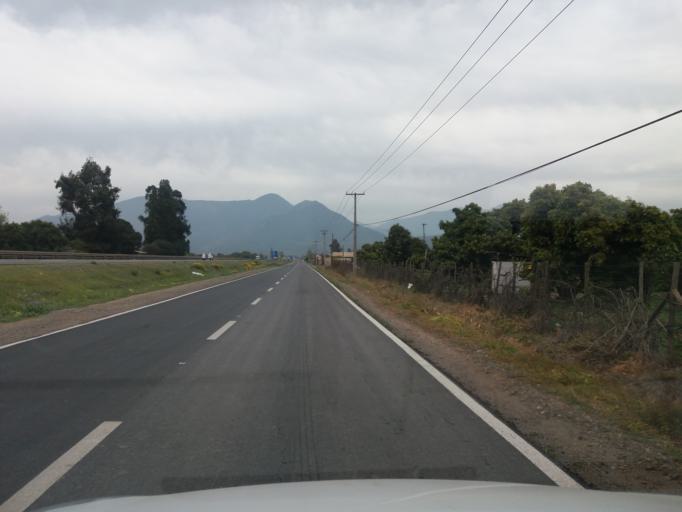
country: CL
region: Valparaiso
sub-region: Provincia de Quillota
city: Hacienda La Calera
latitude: -32.8352
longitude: -71.1199
